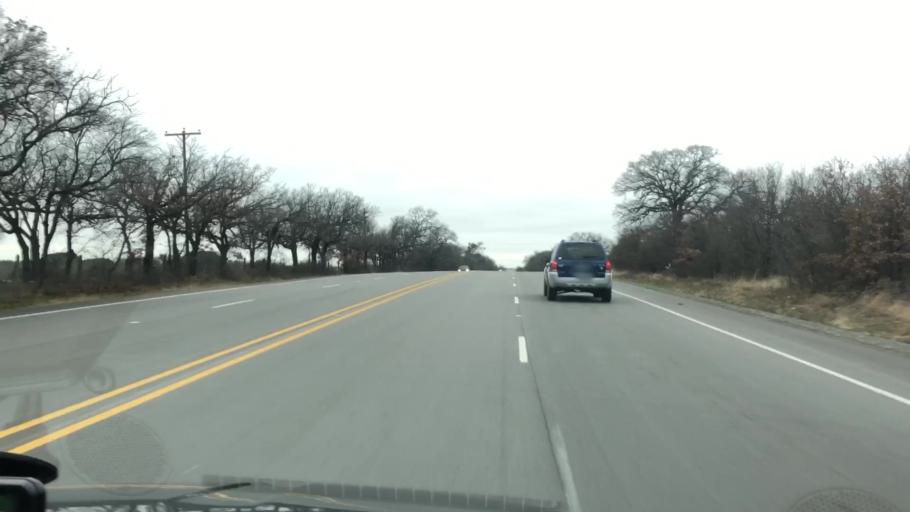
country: US
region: Texas
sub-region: Hamilton County
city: Hico
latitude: 32.0096
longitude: -98.0602
